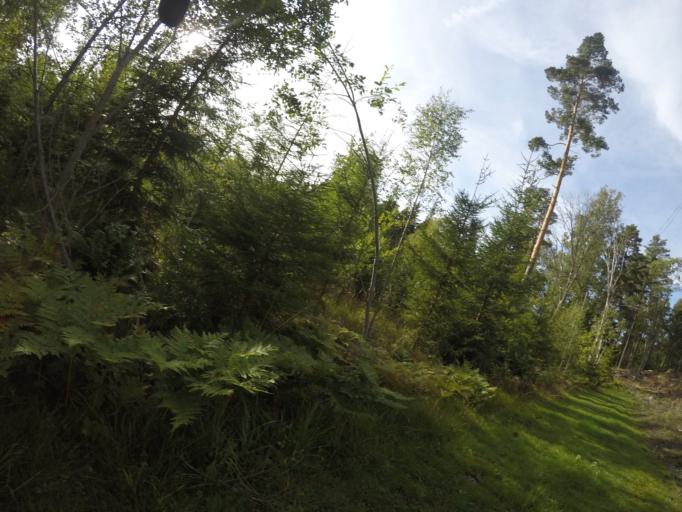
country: SE
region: Soedermanland
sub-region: Eskilstuna Kommun
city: Kvicksund
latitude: 59.5115
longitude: 16.3076
